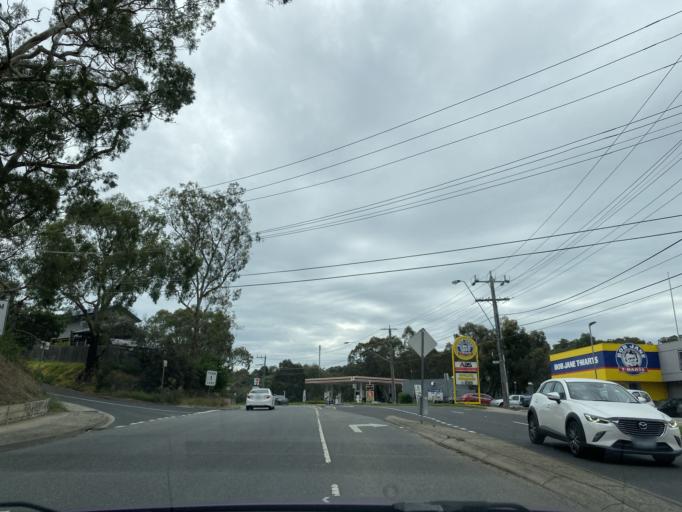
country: AU
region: Victoria
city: Saint Helena
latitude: -37.7172
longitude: 145.1372
